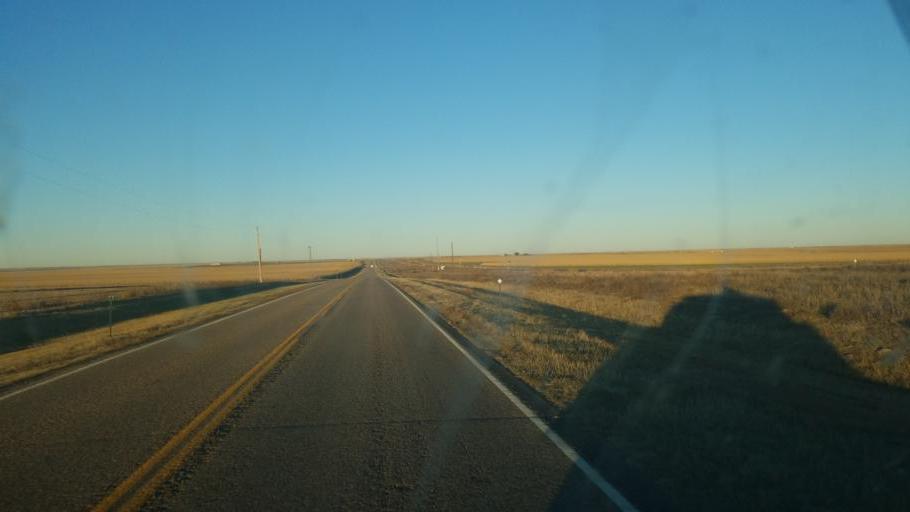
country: US
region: Colorado
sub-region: Cheyenne County
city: Cheyenne Wells
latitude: 38.8514
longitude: -102.0877
